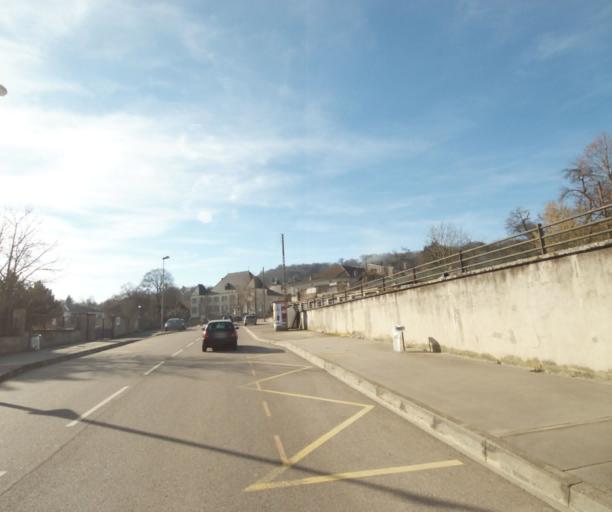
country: FR
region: Lorraine
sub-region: Departement de Meurthe-et-Moselle
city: Vandoeuvre-les-Nancy
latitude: 48.6583
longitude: 6.1703
